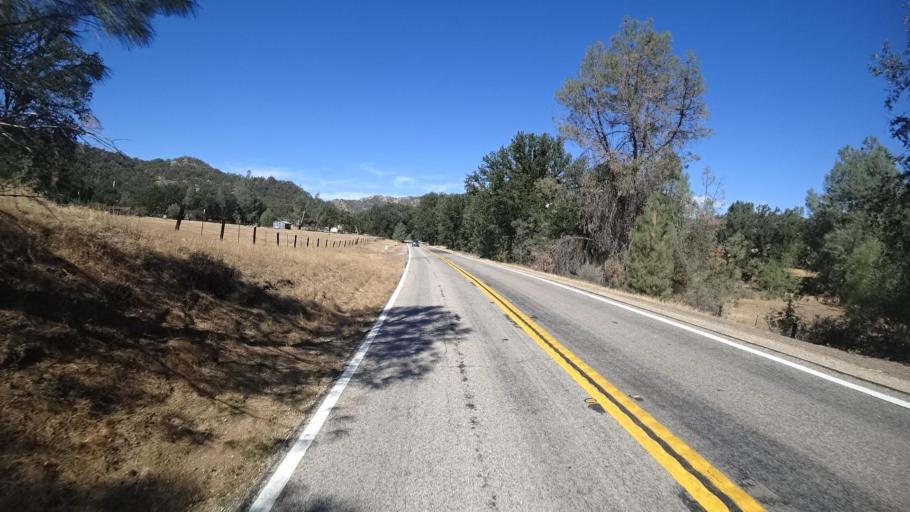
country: US
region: California
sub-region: Fresno County
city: Coalinga
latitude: 36.1989
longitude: -120.7219
